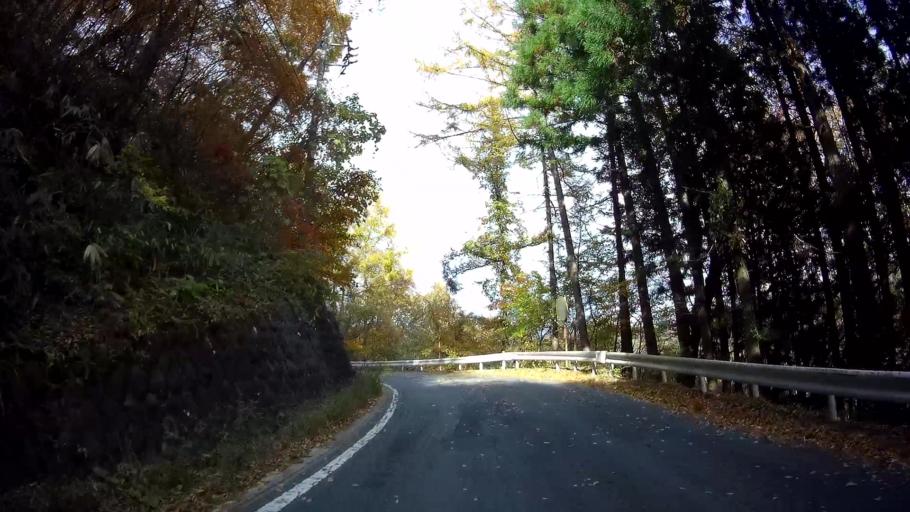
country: JP
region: Gunma
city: Nakanojomachi
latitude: 36.6176
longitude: 138.6383
